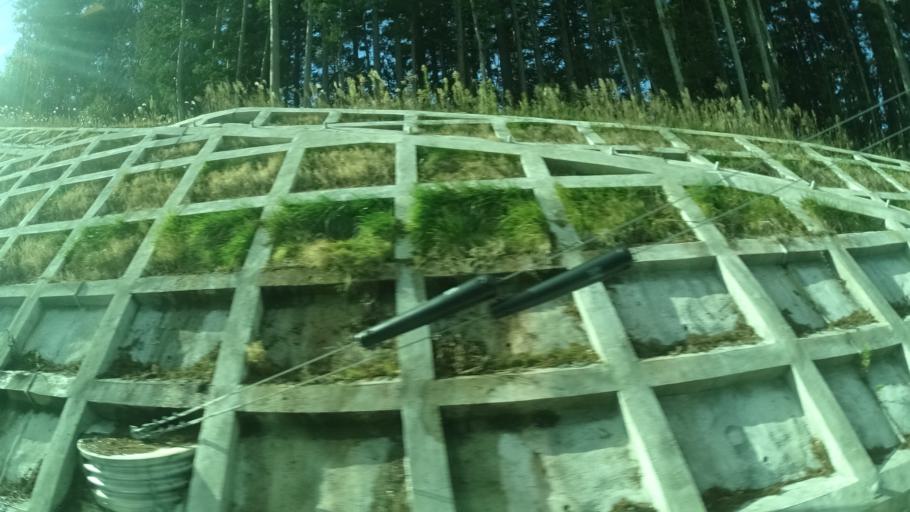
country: JP
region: Miyagi
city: Watari
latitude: 37.9203
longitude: 140.9032
